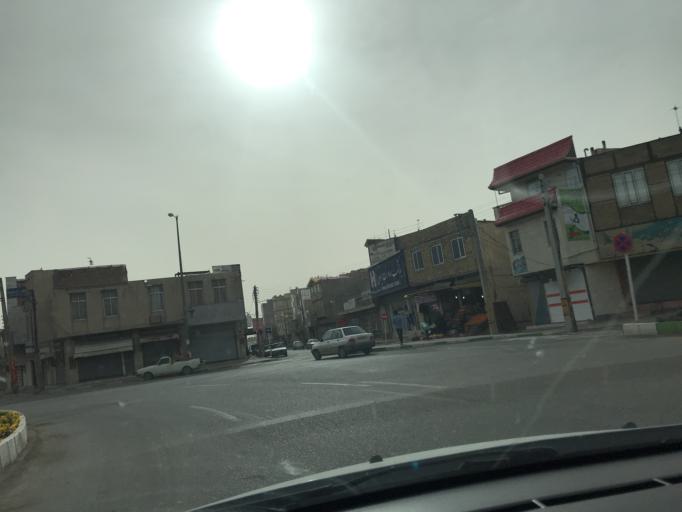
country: IR
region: Qazvin
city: Takestan
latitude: 36.0660
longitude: 49.6897
